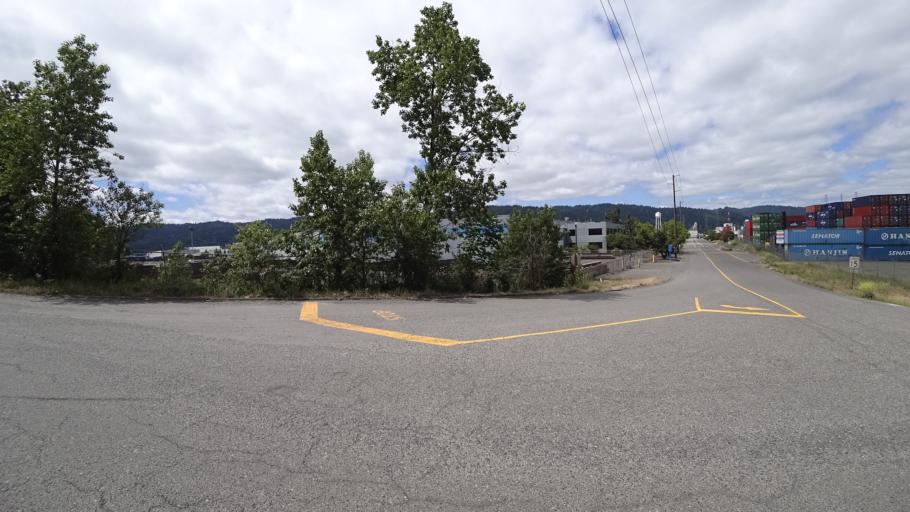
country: US
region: Oregon
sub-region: Washington County
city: West Haven
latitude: 45.6126
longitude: -122.7684
